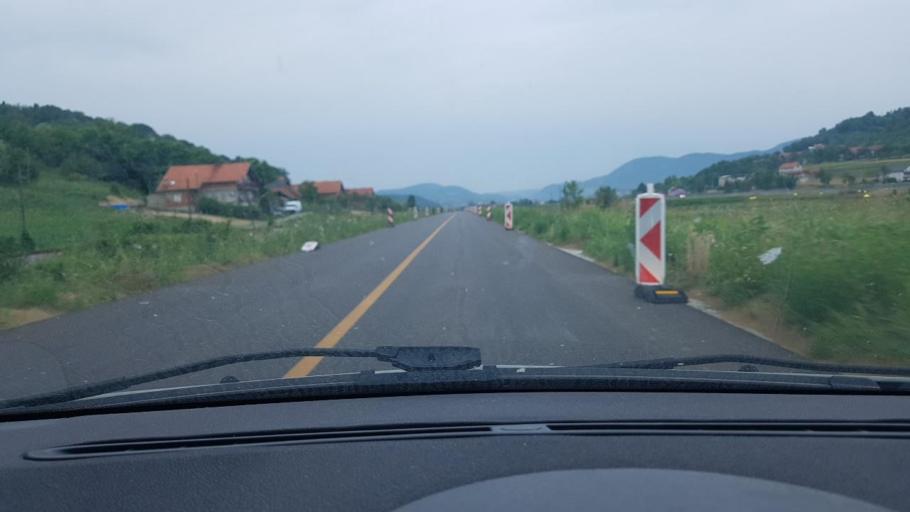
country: HR
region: Krapinsko-Zagorska
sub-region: Grad Krapina
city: Krapina
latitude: 46.1033
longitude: 15.8952
